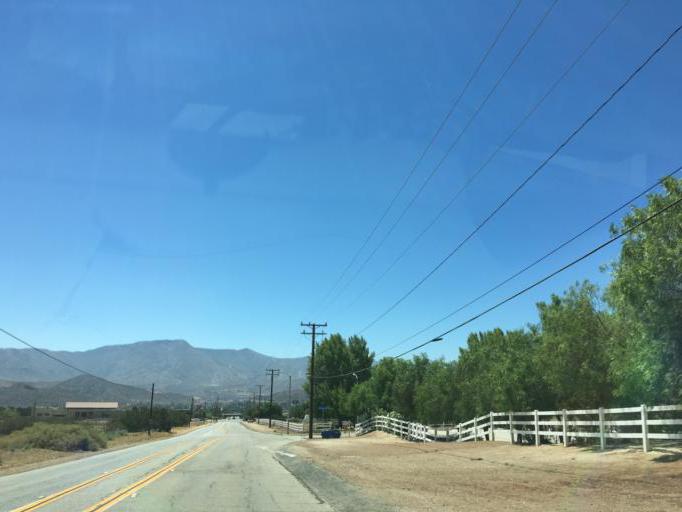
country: US
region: California
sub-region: Los Angeles County
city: Acton
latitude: 34.4984
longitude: -118.1984
